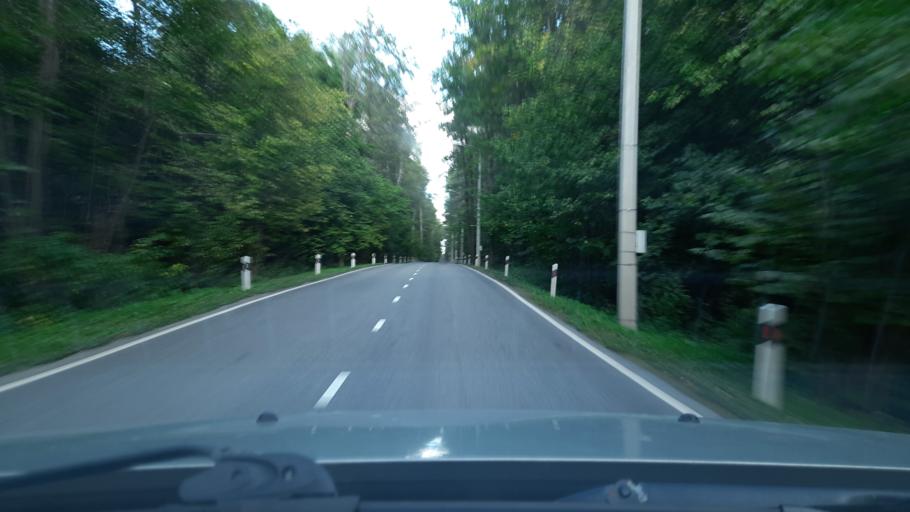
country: RU
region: Moskovskaya
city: Odintsovo
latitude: 55.6967
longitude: 37.2747
